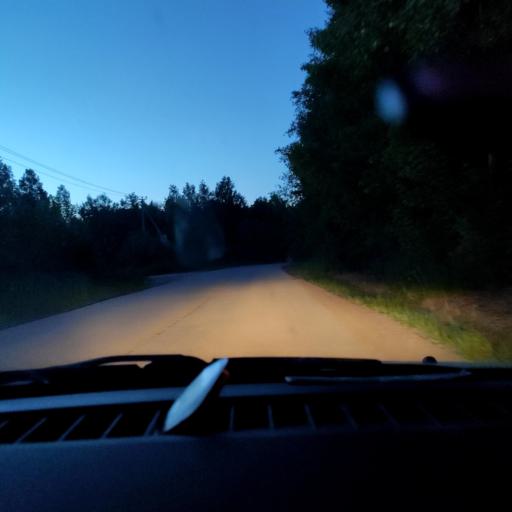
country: RU
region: Perm
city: Kultayevo
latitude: 57.9584
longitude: 55.9108
